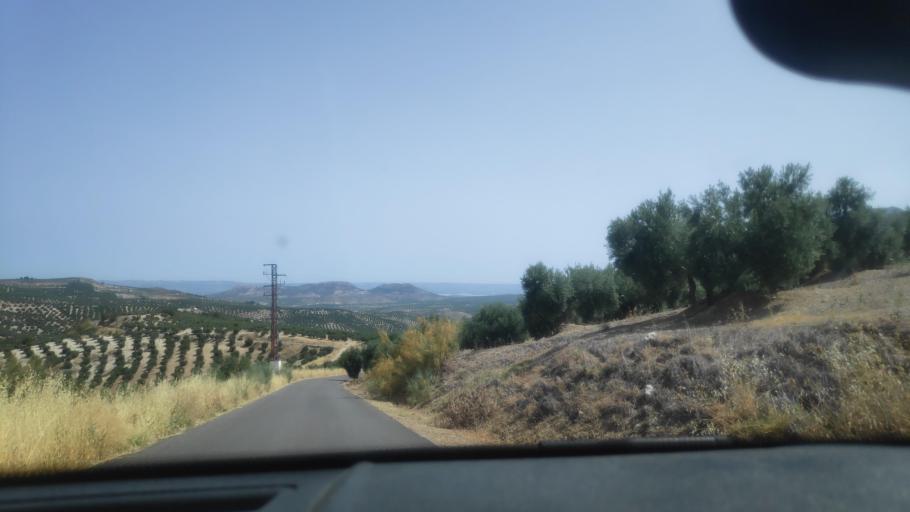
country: ES
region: Andalusia
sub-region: Provincia de Jaen
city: Jimena
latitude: 37.7941
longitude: -3.4493
